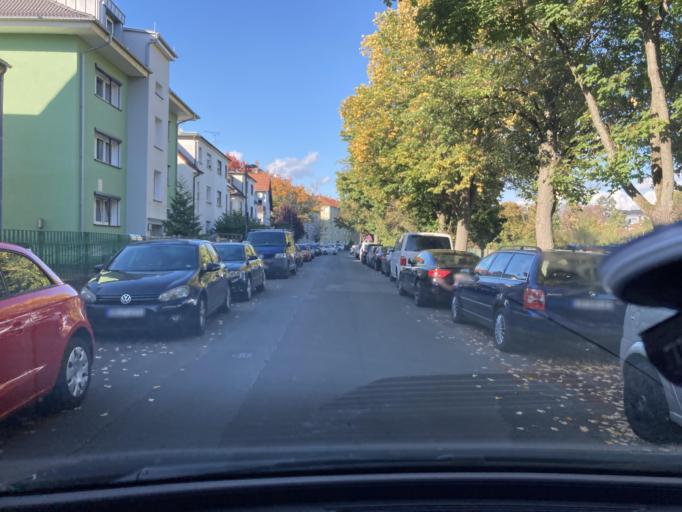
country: DE
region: Hesse
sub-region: Regierungsbezirk Darmstadt
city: Offenbach
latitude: 50.0925
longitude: 8.7710
